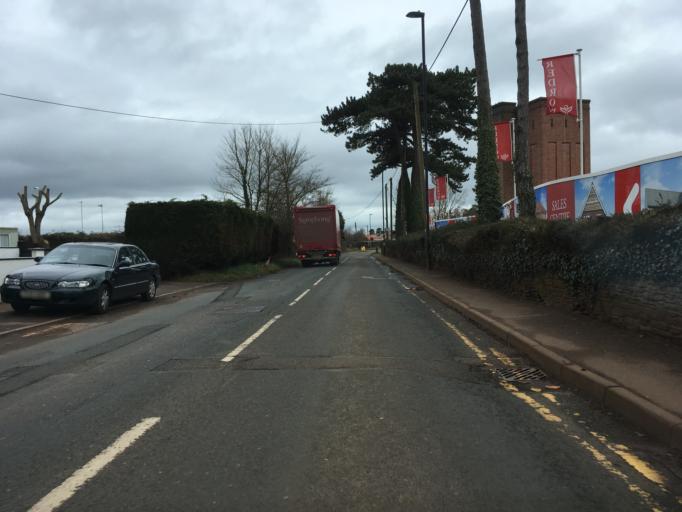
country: GB
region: England
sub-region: South Gloucestershire
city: Stoke Gifford
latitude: 51.4975
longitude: -2.5283
